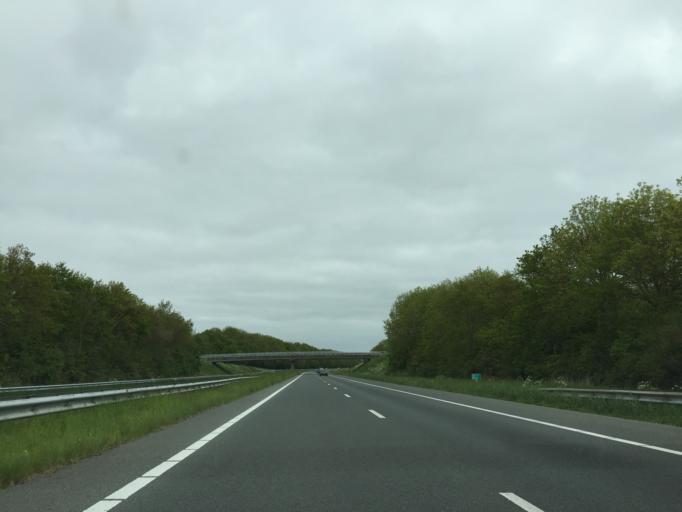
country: NL
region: North Holland
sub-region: Gemeente Hollands Kroon
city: Den Oever
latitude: 52.8940
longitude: 5.0261
